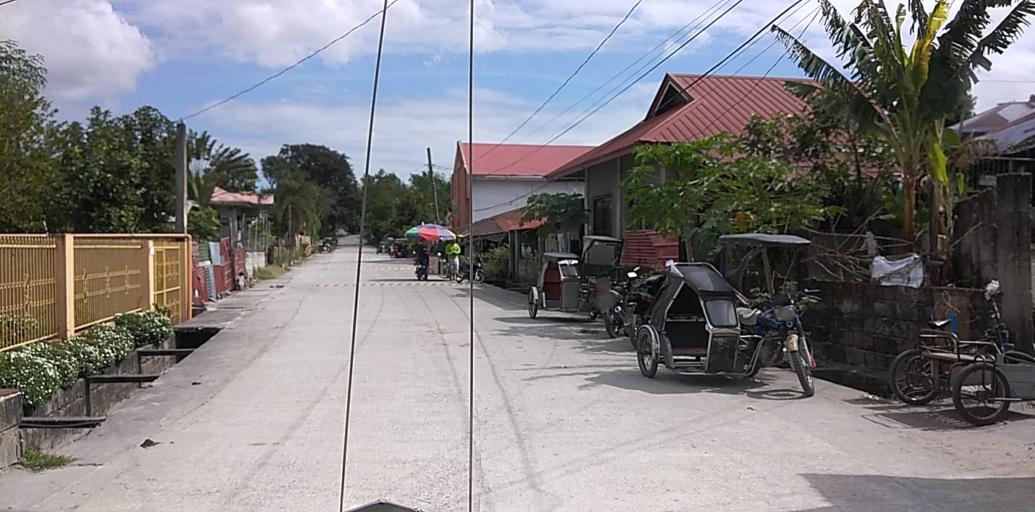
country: PH
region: Central Luzon
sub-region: Province of Pampanga
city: Porac
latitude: 15.0650
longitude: 120.5365
